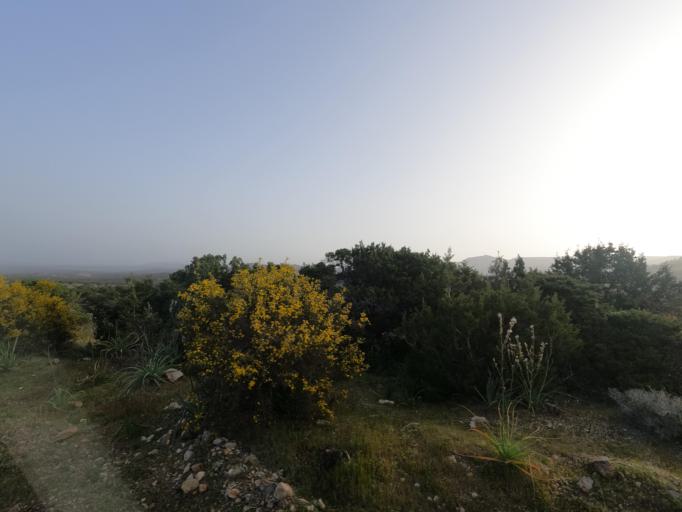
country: CY
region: Pafos
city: Pegeia
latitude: 34.9779
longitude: 32.3178
